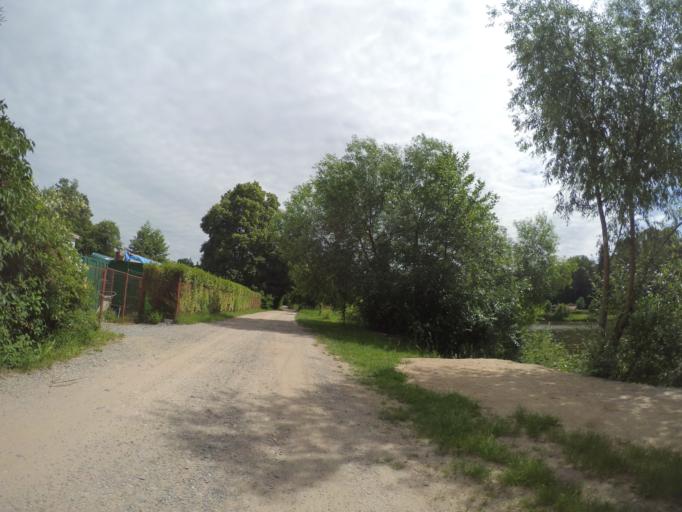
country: CZ
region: Central Bohemia
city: Lysa nad Labem
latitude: 50.1752
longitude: 14.8593
